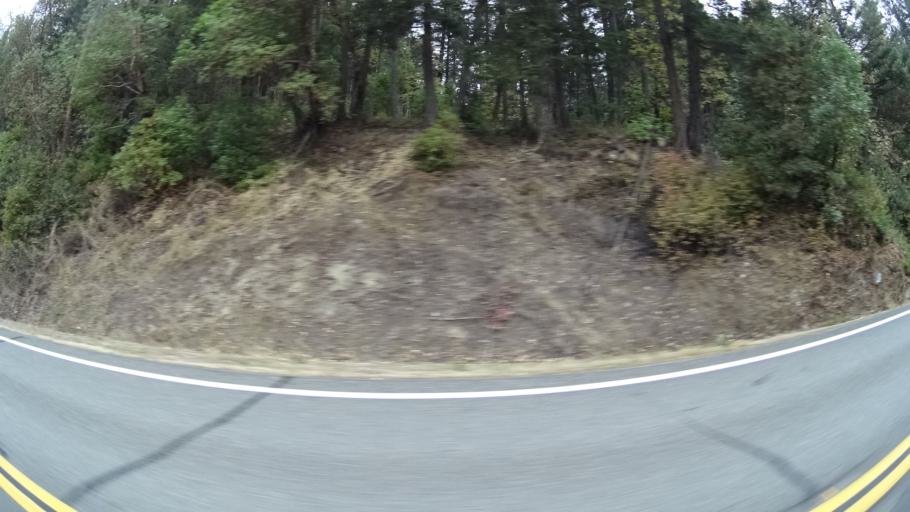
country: US
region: California
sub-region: Siskiyou County
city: Happy Camp
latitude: 41.8116
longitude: -123.3556
